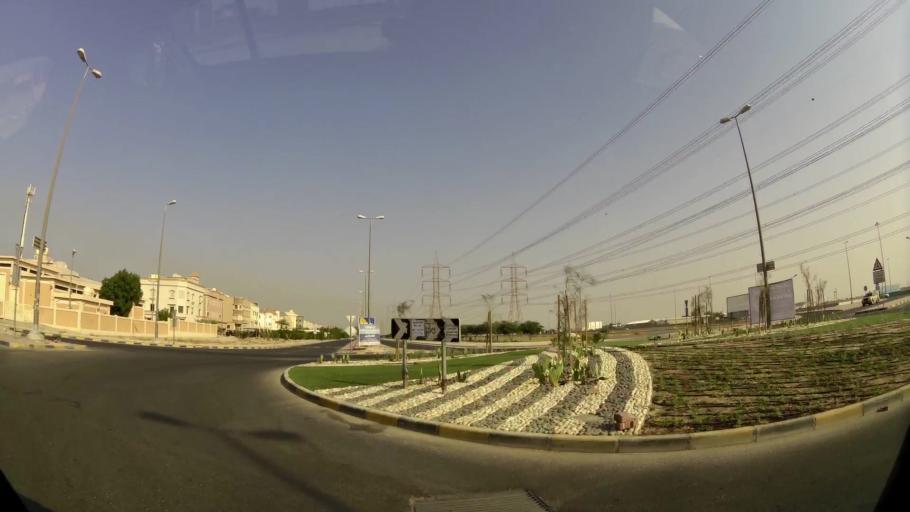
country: KW
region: Al Asimah
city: Ar Rabiyah
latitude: 29.2973
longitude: 47.8007
